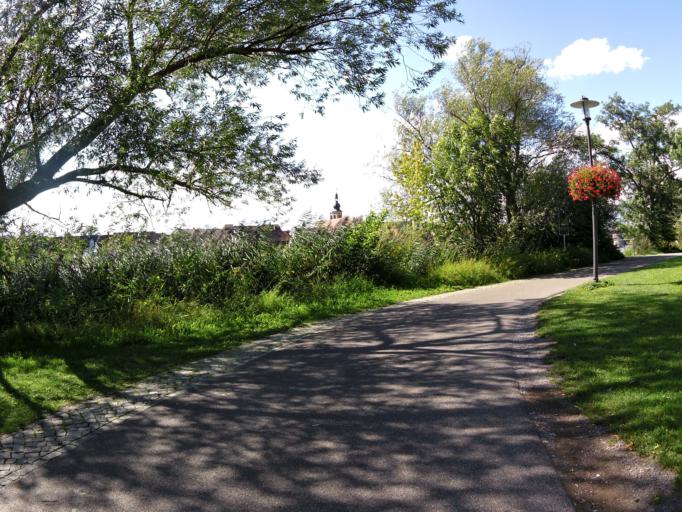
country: DE
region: Bavaria
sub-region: Regierungsbezirk Unterfranken
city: Kitzingen
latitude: 49.7376
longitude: 10.1677
